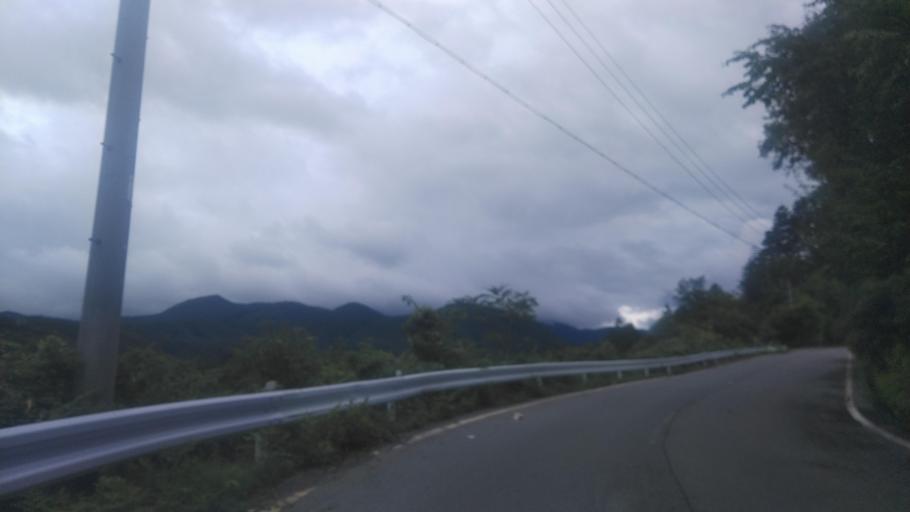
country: JP
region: Nagano
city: Ueda
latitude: 36.4976
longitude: 138.3857
